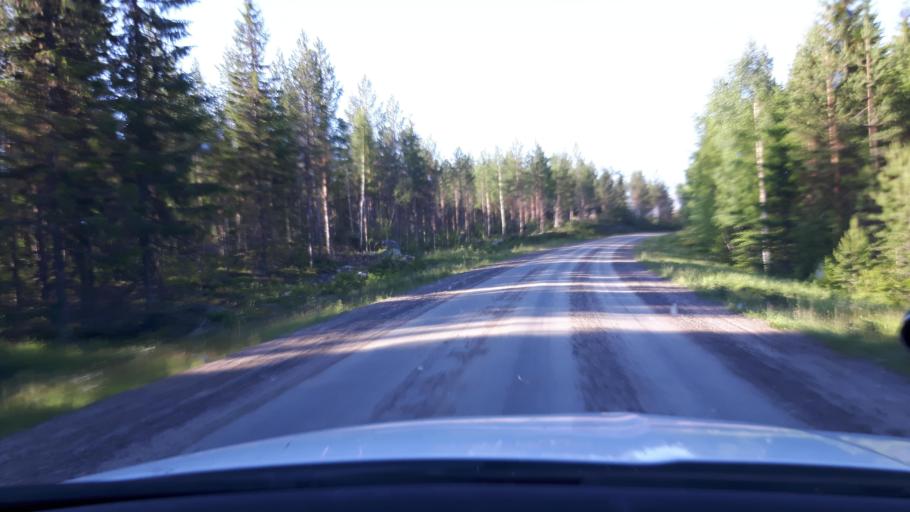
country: SE
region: Gaevleborg
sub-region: Ljusdals Kommun
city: Farila
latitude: 62.0141
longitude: 15.8394
